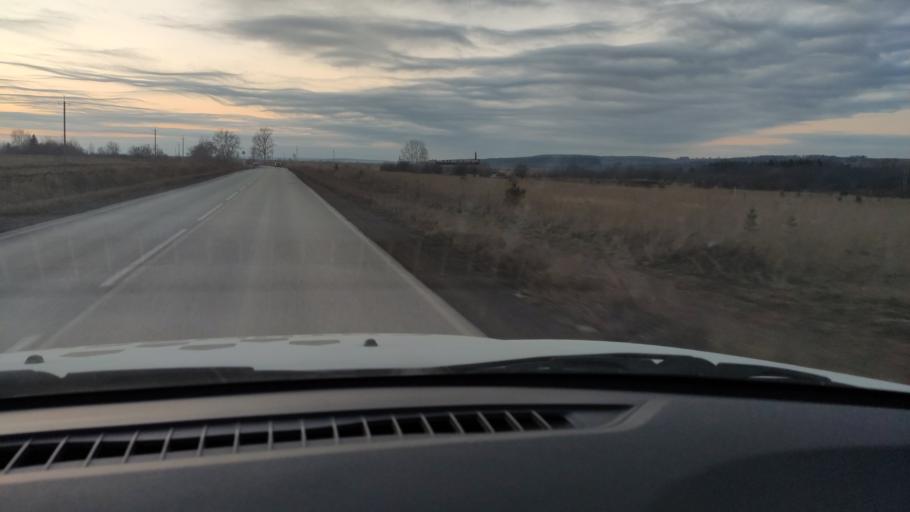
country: RU
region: Perm
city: Lobanovo
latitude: 57.8074
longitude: 56.3544
